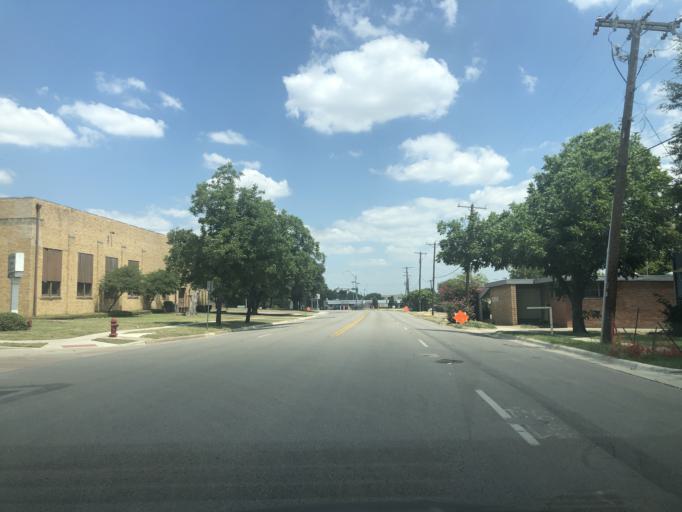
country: US
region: Texas
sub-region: Dallas County
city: Grand Prairie
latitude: 32.7476
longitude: -97.0052
